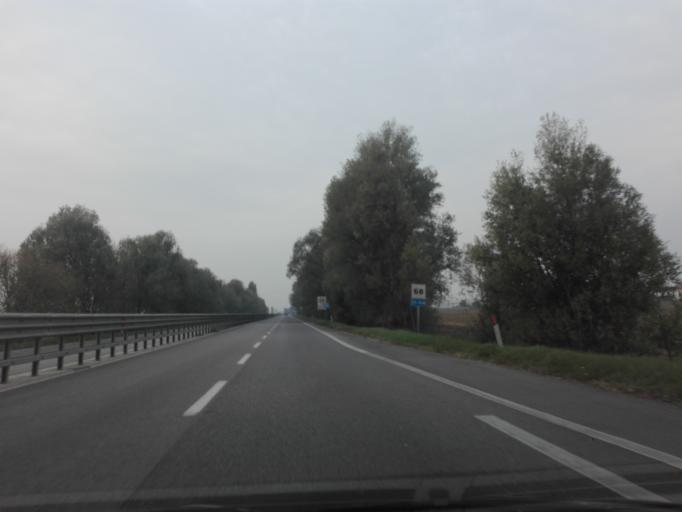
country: IT
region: Veneto
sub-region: Provincia di Rovigo
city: San Bellino
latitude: 45.0256
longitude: 11.5854
